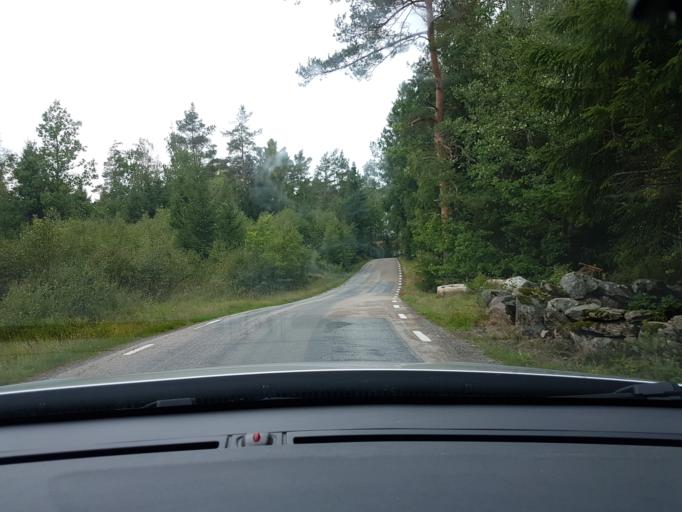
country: SE
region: Vaestra Goetaland
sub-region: Ale Kommun
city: Alvangen
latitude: 57.9096
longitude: 12.1591
